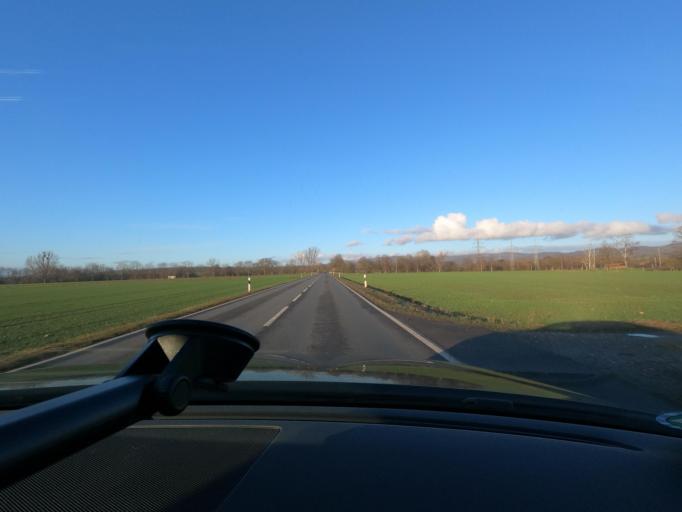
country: DE
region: Lower Saxony
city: Rhumspringe
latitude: 51.6173
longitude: 10.3221
